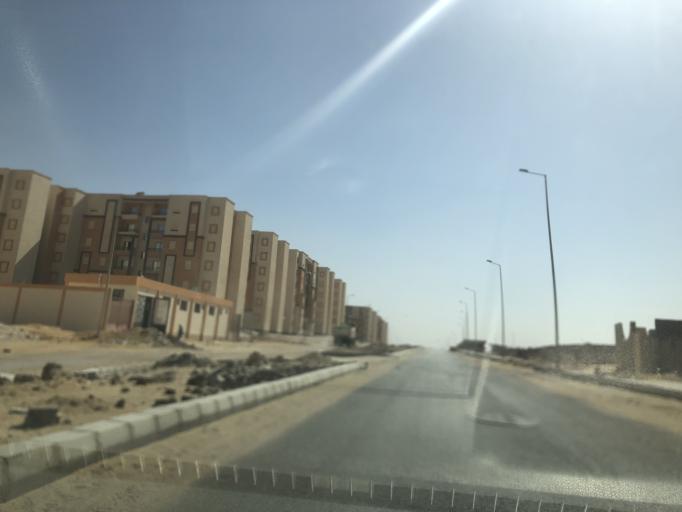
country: EG
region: Al Jizah
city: Madinat Sittah Uktubar
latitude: 29.9338
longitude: 30.9736
